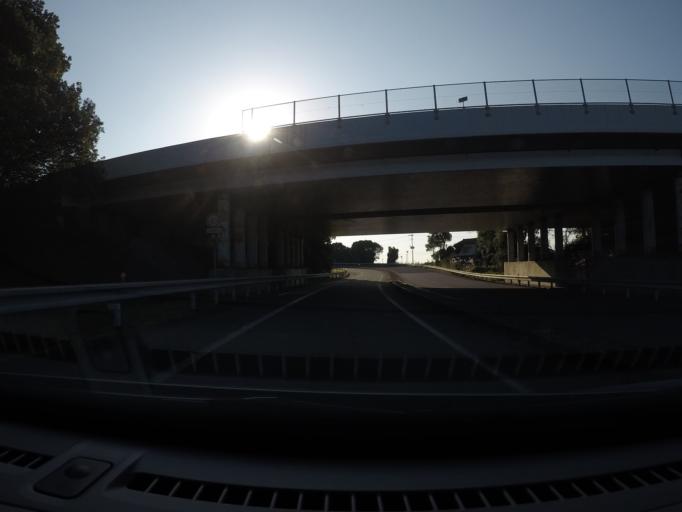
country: JP
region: Kagoshima
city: Kokubu-matsuki
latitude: 31.7898
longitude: 130.7178
